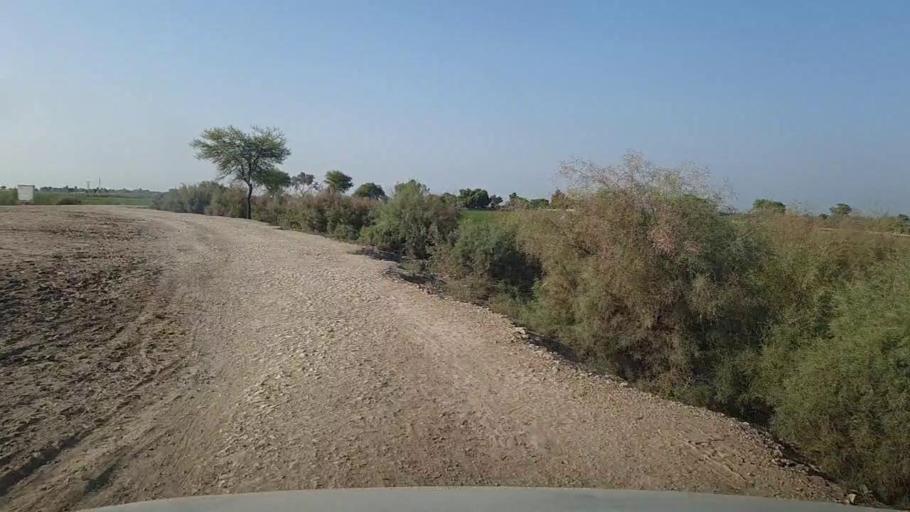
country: PK
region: Sindh
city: Kandhkot
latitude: 28.2976
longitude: 69.3292
